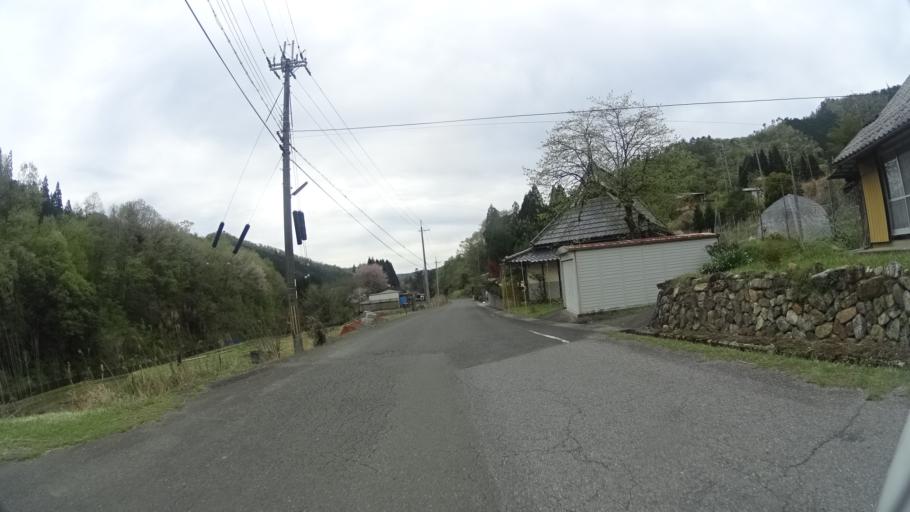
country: JP
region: Kyoto
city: Ayabe
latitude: 35.2213
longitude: 135.4723
